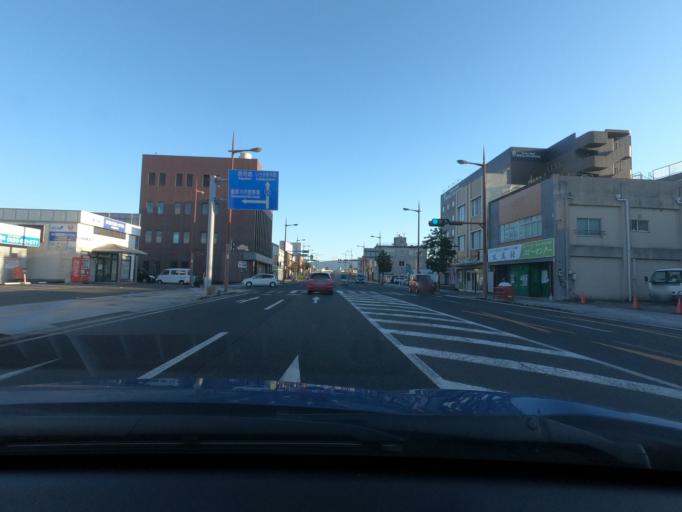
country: JP
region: Kagoshima
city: Satsumasendai
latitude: 31.8225
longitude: 130.3024
